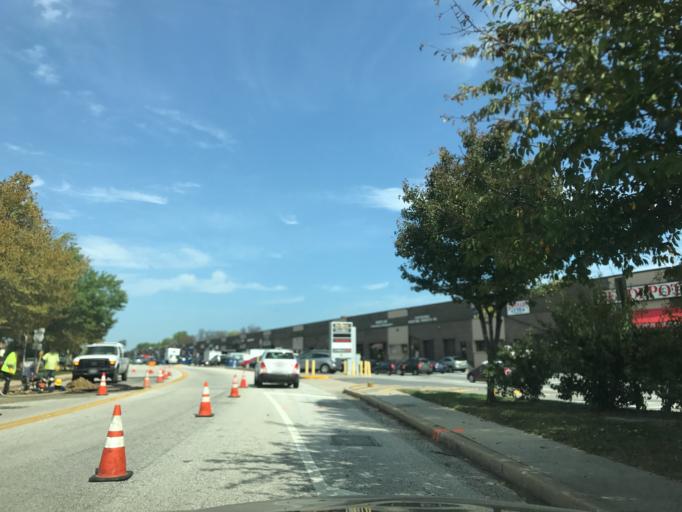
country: US
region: Maryland
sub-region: Baltimore County
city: Timonium
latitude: 39.4412
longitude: -76.6322
